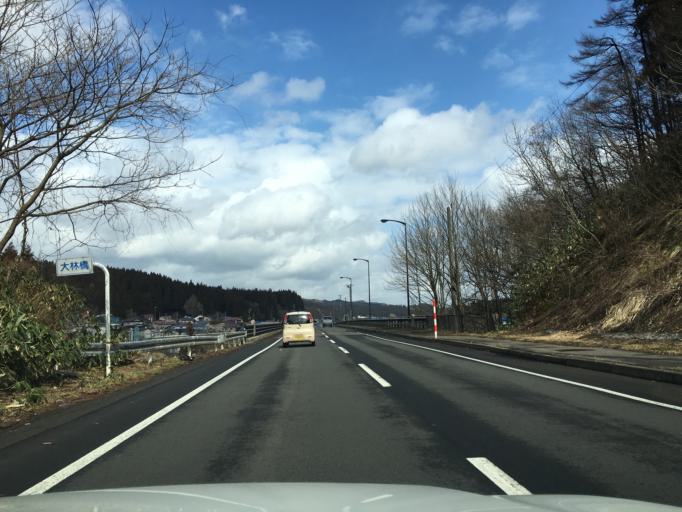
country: JP
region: Akita
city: Takanosu
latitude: 40.0291
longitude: 140.2740
